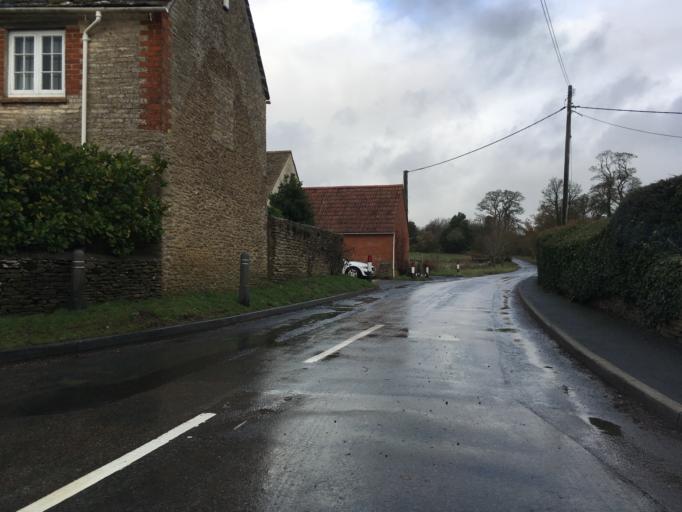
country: GB
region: England
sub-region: Gloucestershire
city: Tetbury
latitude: 51.6266
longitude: -2.1337
